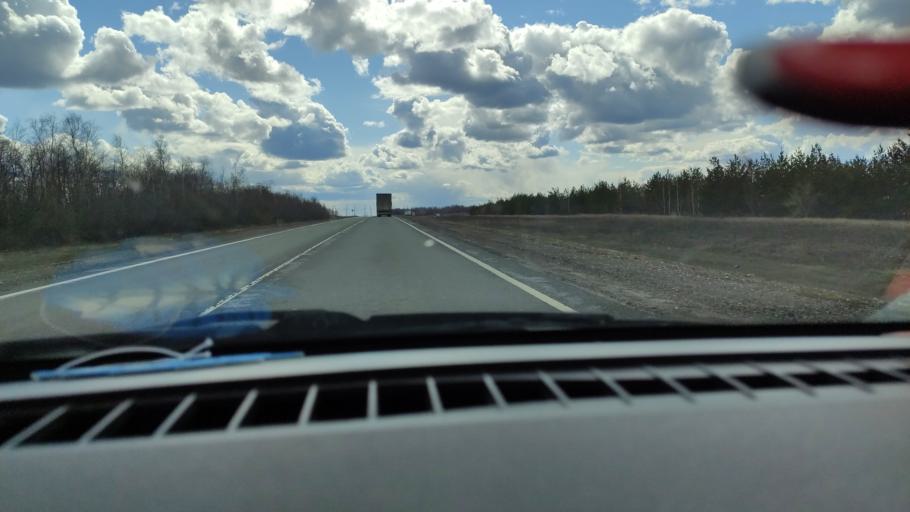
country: RU
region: Samara
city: Syzran'
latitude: 52.8688
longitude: 48.2810
